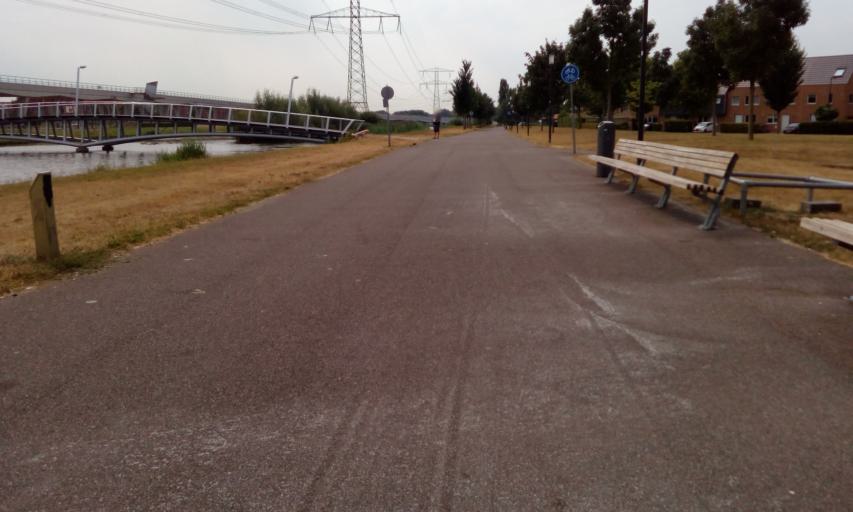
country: NL
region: South Holland
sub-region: Gemeente Capelle aan den IJssel
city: Capelle aan den IJssel
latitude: 51.9758
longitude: 4.5847
